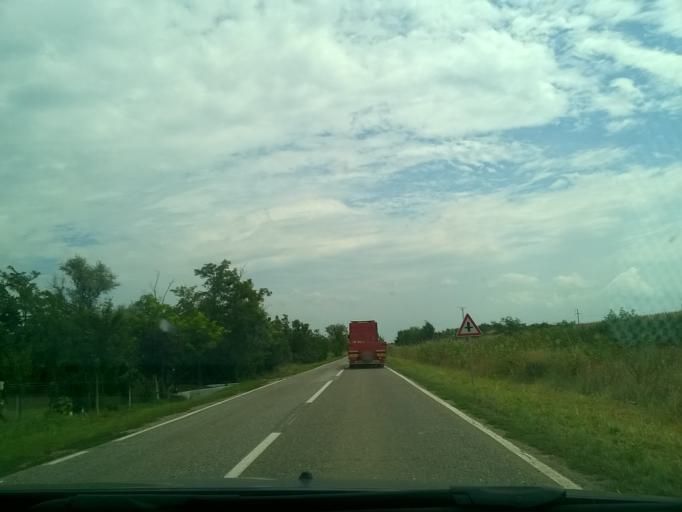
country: RS
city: Klek
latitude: 45.3869
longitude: 20.4900
